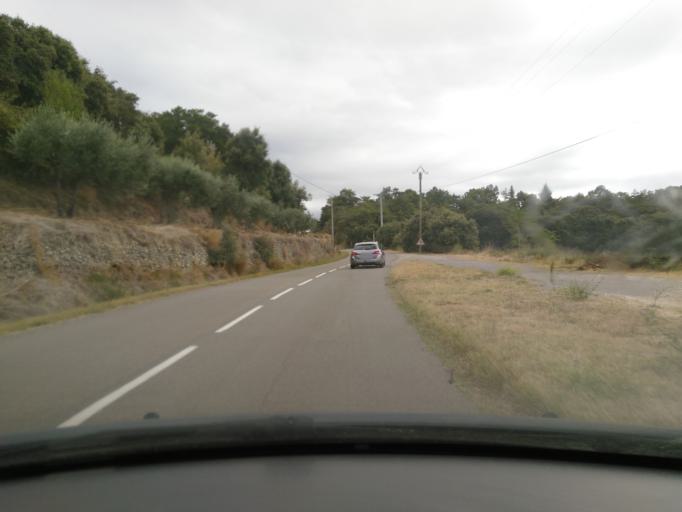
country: FR
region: Provence-Alpes-Cote d'Azur
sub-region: Departement du Vaucluse
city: Valreas
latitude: 44.4171
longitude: 5.0662
